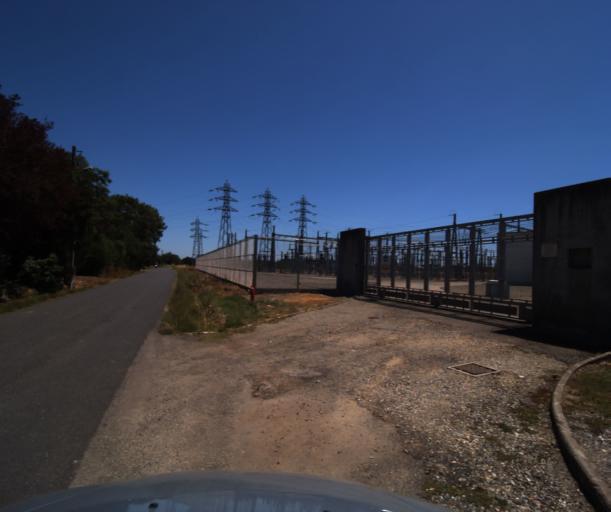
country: FR
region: Midi-Pyrenees
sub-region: Departement de la Haute-Garonne
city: Muret
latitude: 43.4483
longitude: 1.3412
